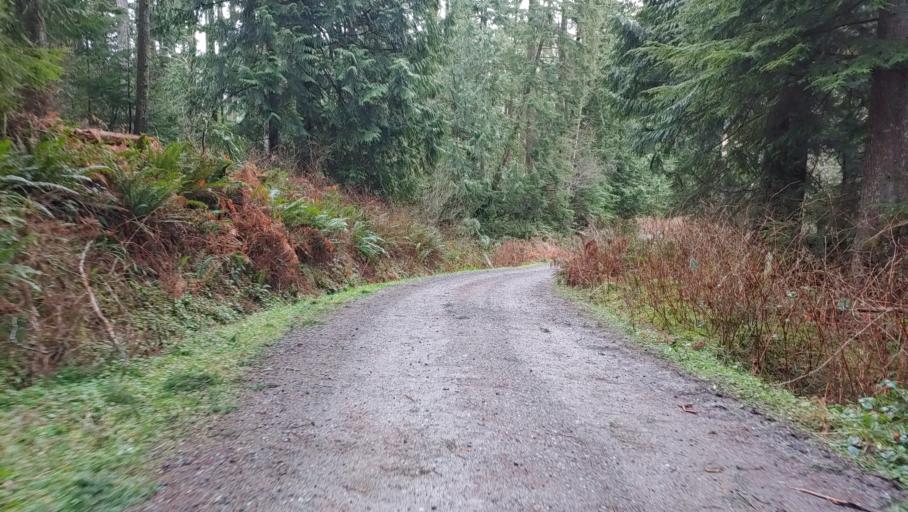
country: US
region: Washington
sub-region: King County
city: Hobart
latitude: 47.4676
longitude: -121.9293
